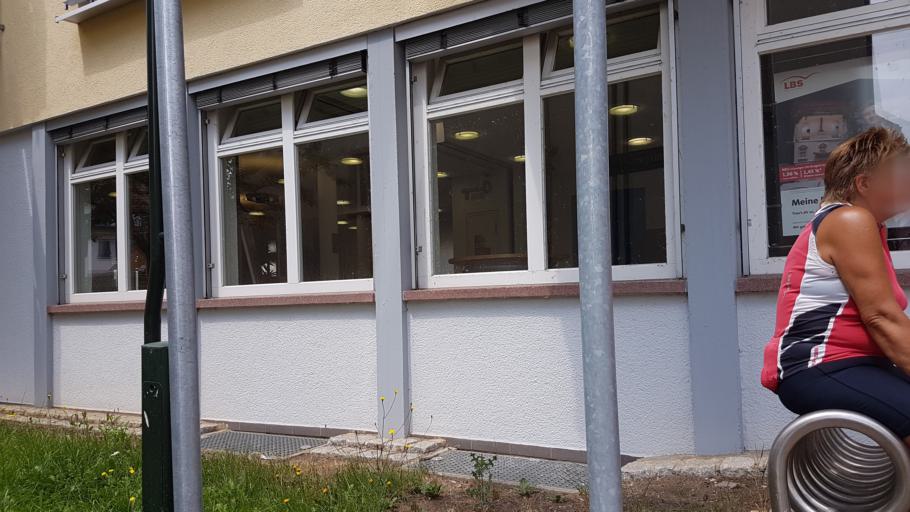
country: DE
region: Baden-Wuerttemberg
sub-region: Freiburg Region
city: Hufingen
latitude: 47.9264
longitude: 8.4894
